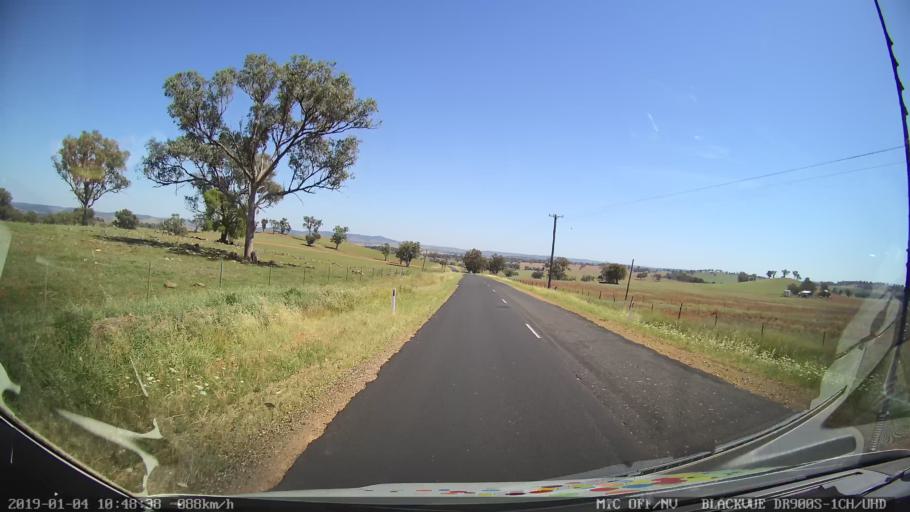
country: AU
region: New South Wales
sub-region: Cabonne
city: Molong
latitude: -33.2575
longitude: 148.7122
